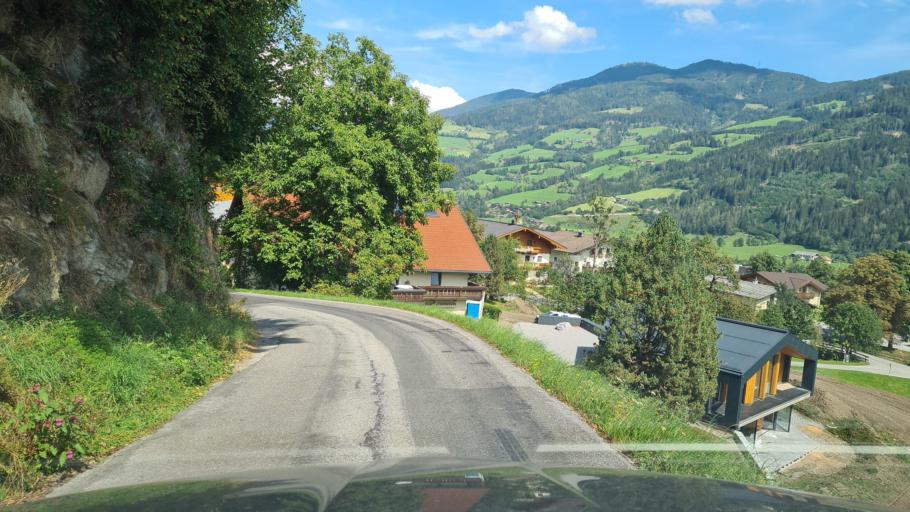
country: AT
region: Salzburg
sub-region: Politischer Bezirk Sankt Johann im Pongau
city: Sankt Johann im Pongau
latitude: 47.3600
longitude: 13.1952
